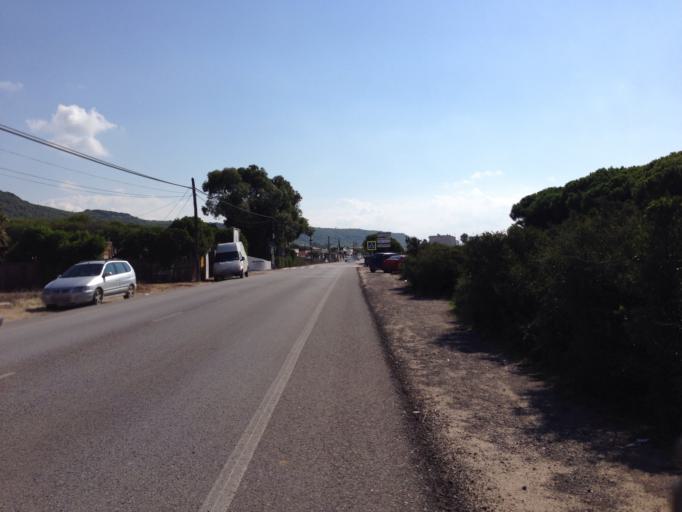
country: ES
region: Andalusia
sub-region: Provincia de Cadiz
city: Vejer de la Frontera
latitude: 36.1879
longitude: -6.0217
